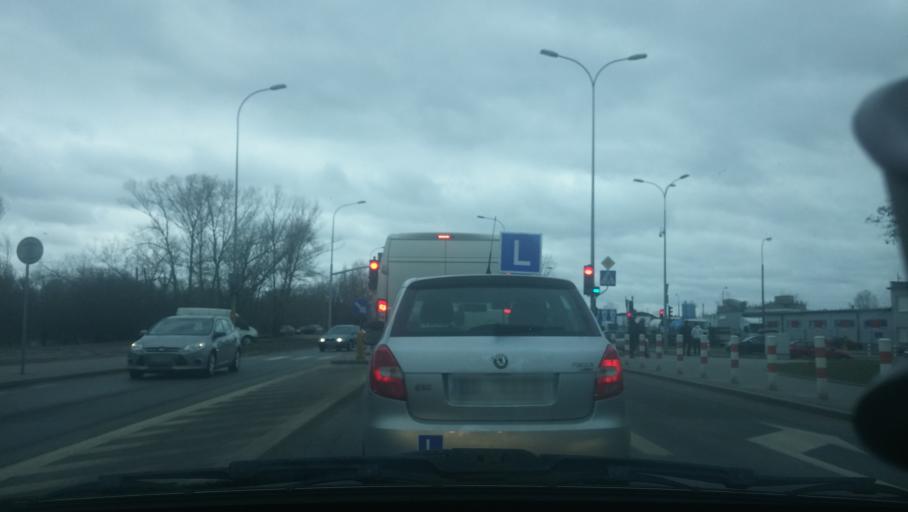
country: PL
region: Masovian Voivodeship
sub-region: Warszawa
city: Bialoleka
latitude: 52.3170
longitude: 21.0133
